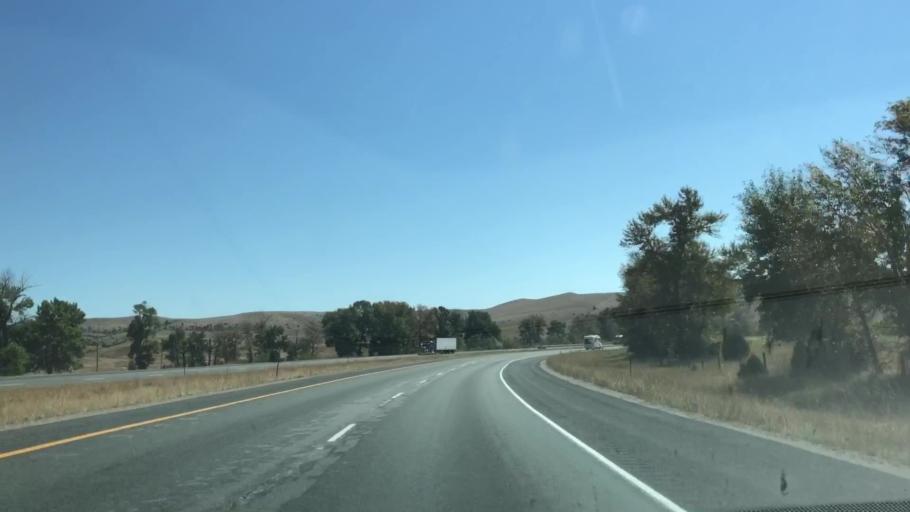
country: US
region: Montana
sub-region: Powell County
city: Deer Lodge
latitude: 46.5388
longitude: -112.8287
